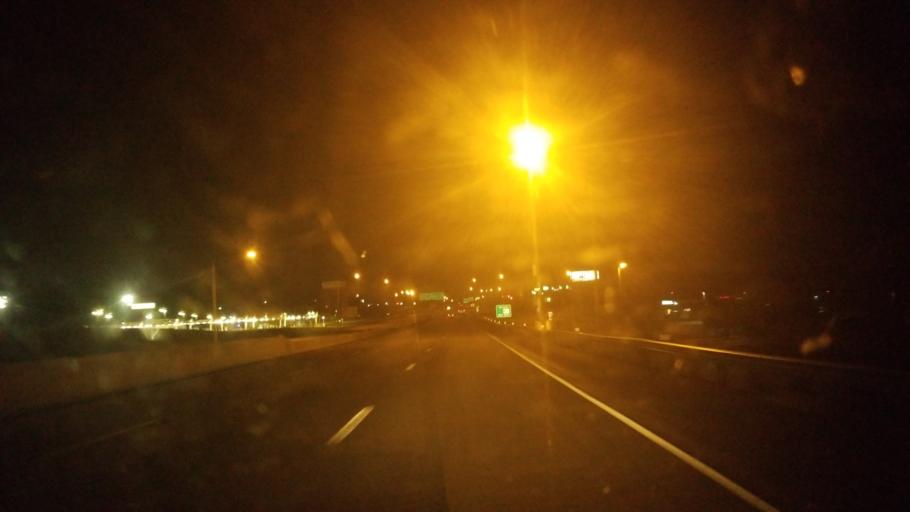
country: US
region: Missouri
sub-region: Saint Louis County
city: Black Jack
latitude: 38.7712
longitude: -90.2703
